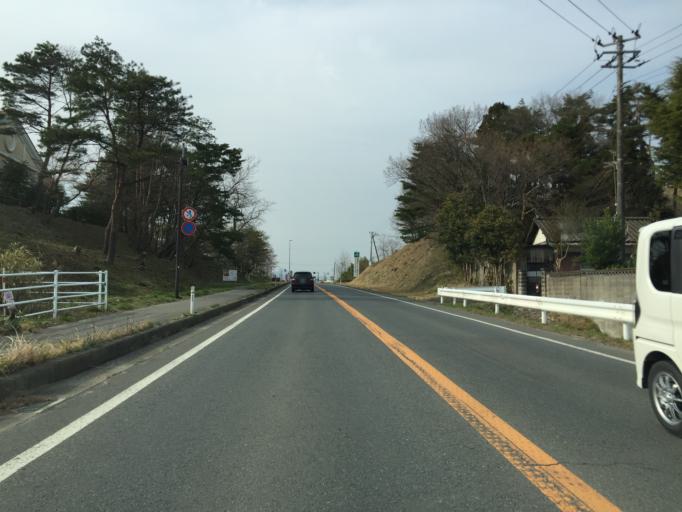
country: JP
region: Miyagi
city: Marumori
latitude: 37.7823
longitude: 140.9360
